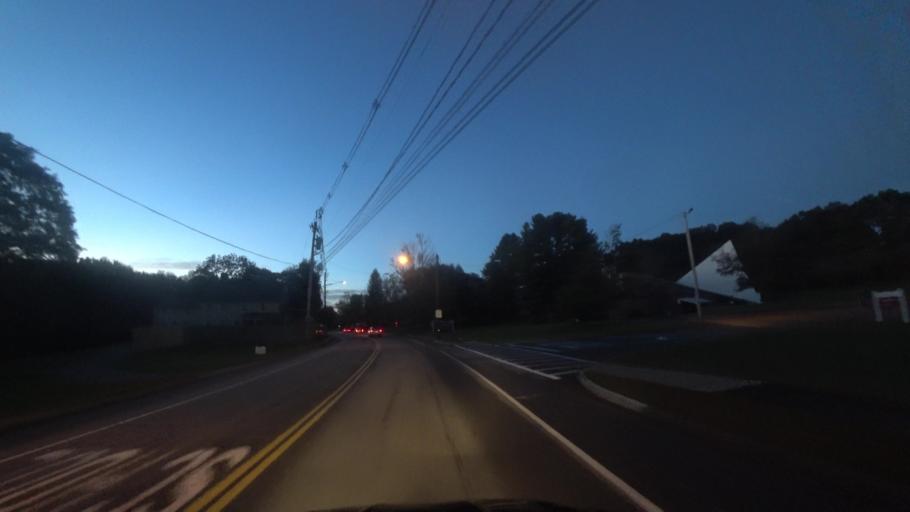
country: US
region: Massachusetts
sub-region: Middlesex County
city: Reading
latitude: 42.5402
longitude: -71.0884
